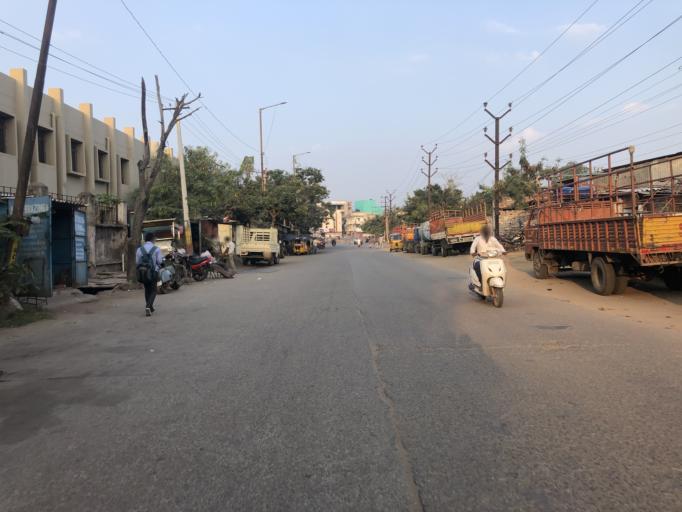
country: IN
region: Telangana
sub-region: Rangareddi
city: Kukatpalli
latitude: 17.4657
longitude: 78.4446
